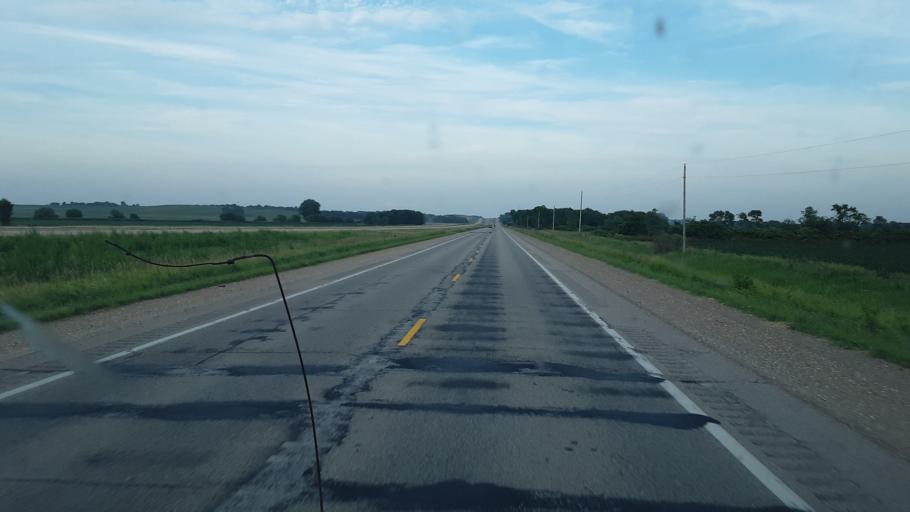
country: US
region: Iowa
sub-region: Tama County
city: Tama
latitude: 41.9638
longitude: -92.4855
